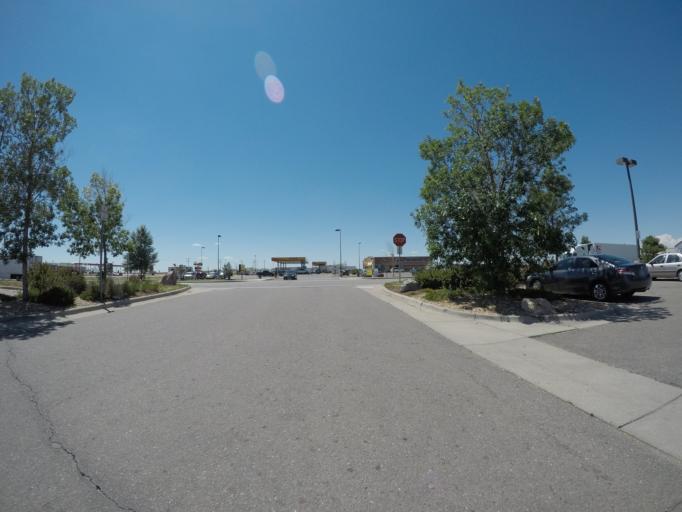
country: US
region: Colorado
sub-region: Adams County
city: Bennett
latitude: 39.7424
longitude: -104.4343
